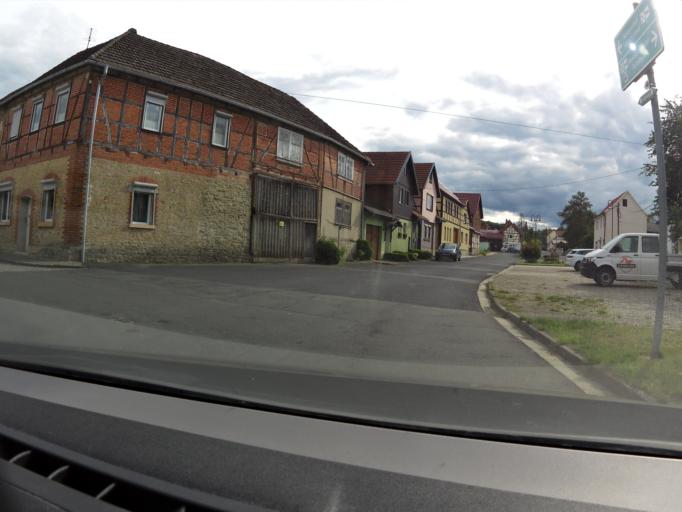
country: DE
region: Thuringia
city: Kammerforst
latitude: 51.1218
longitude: 10.4217
